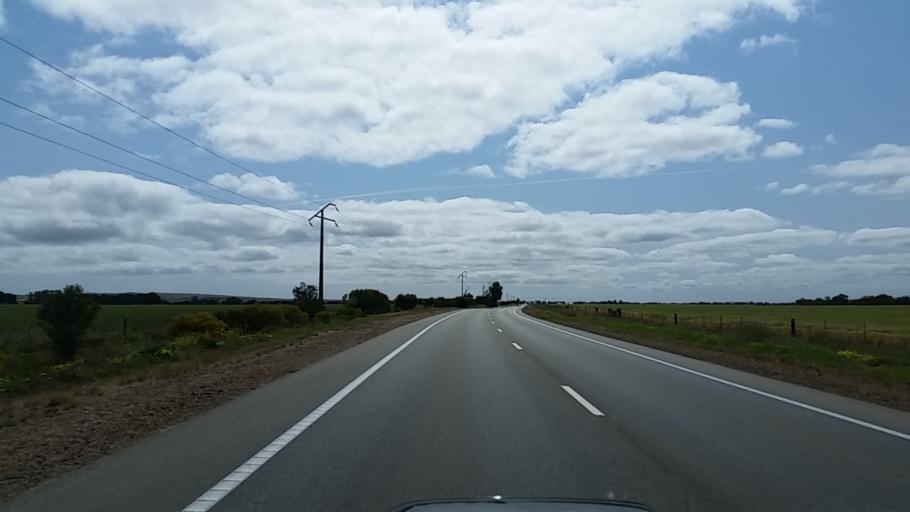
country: AU
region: South Australia
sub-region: Port Pirie City and Dists
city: Crystal Brook
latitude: -33.4816
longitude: 138.1723
